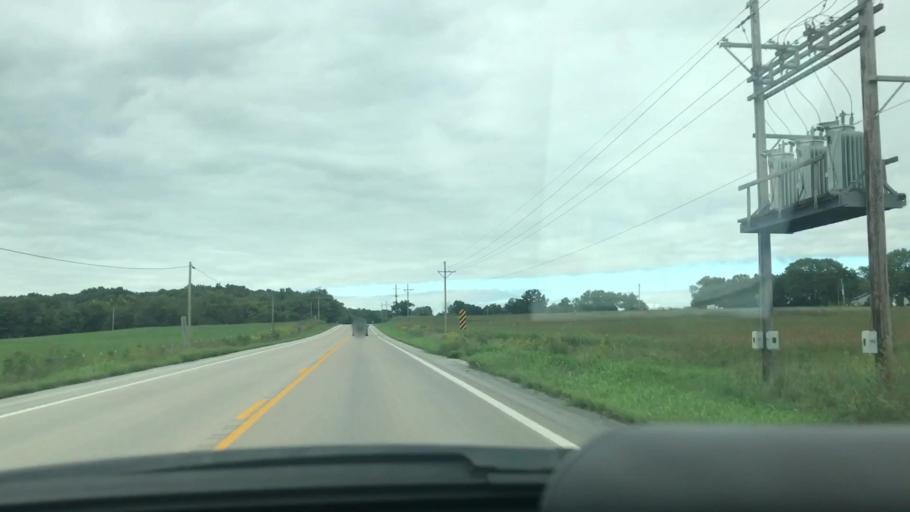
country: US
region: Missouri
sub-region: Hickory County
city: Hermitage
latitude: 37.8654
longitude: -93.1789
